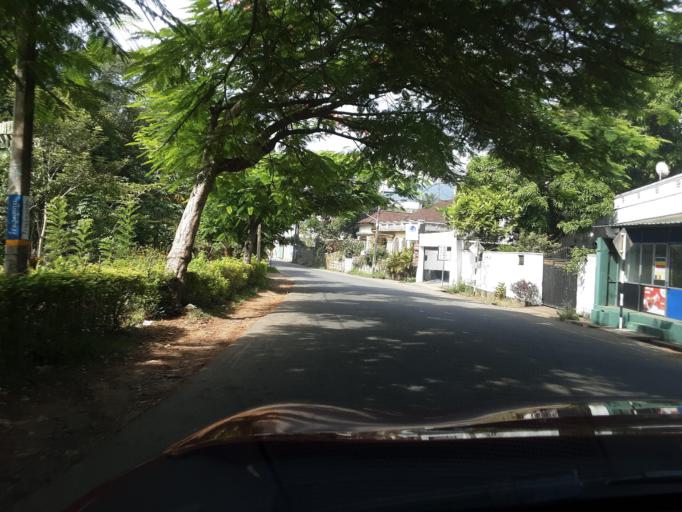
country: LK
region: Uva
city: Badulla
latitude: 6.9877
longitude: 81.0638
